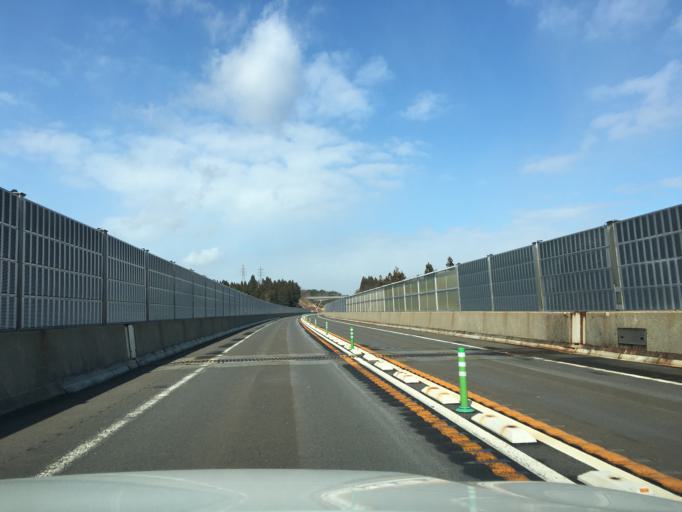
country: JP
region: Akita
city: Akita
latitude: 39.7548
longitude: 140.1390
